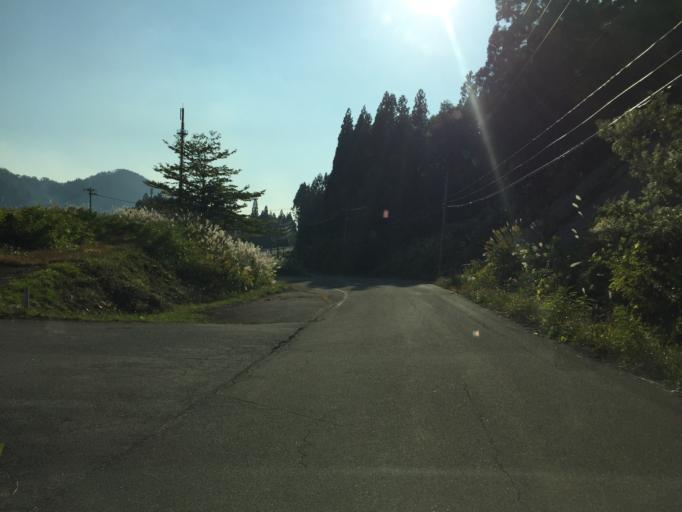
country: JP
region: Fukushima
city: Kitakata
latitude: 37.7488
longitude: 139.8986
